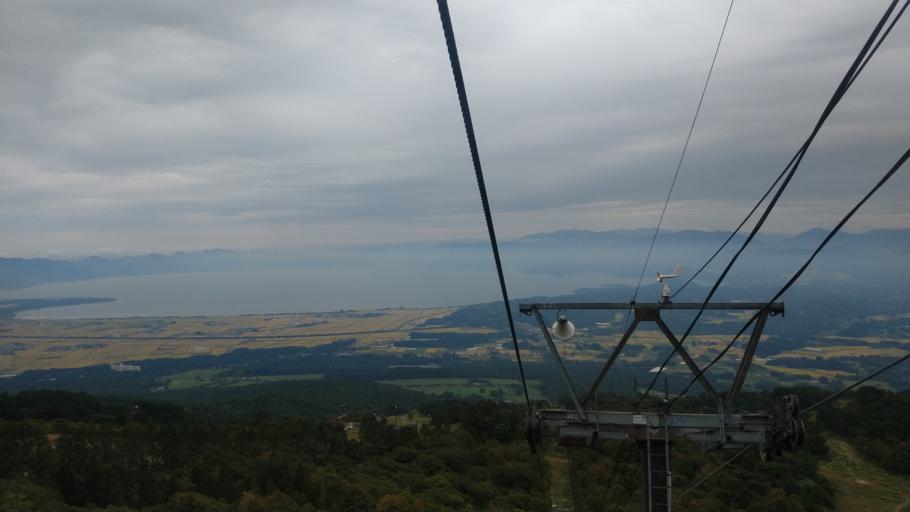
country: JP
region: Fukushima
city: Inawashiro
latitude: 37.5932
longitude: 140.0629
